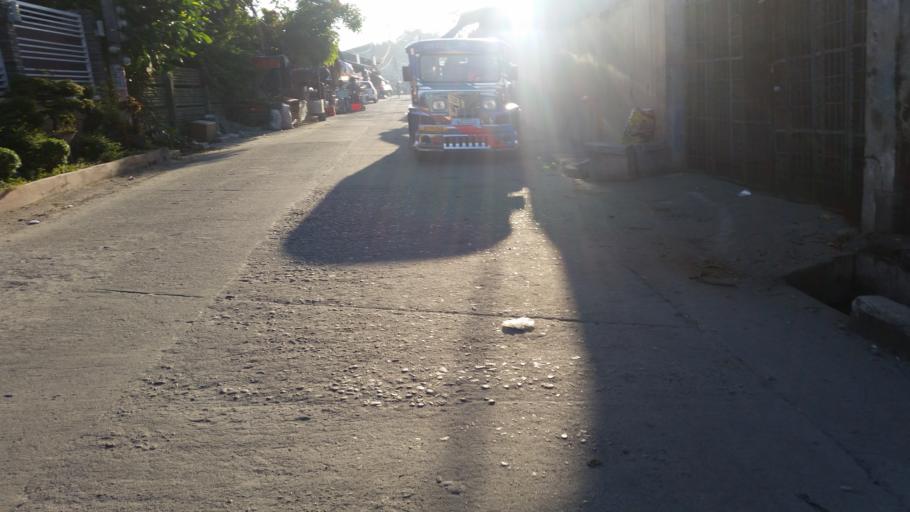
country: PH
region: Central Luzon
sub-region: Province of Pampanga
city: Mabalacat City
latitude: 15.2744
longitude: 120.5663
